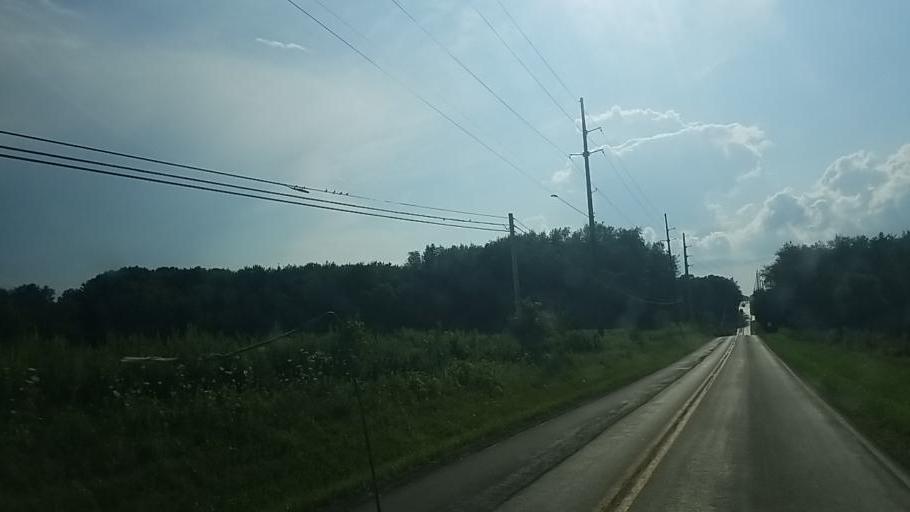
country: US
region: Ohio
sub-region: Wayne County
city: Wooster
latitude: 40.8580
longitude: -81.9593
